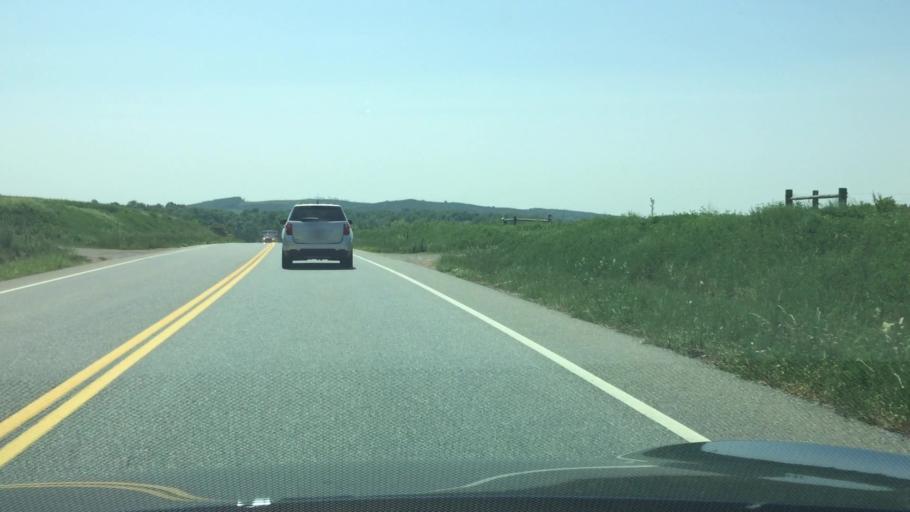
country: US
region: Virginia
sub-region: Campbell County
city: Altavista
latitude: 37.1979
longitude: -79.2993
